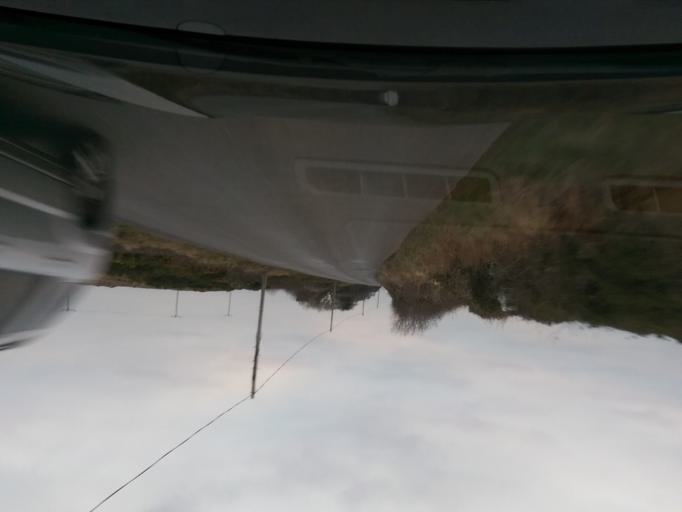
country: IE
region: Connaught
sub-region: County Galway
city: Bearna
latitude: 53.2714
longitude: -9.1594
